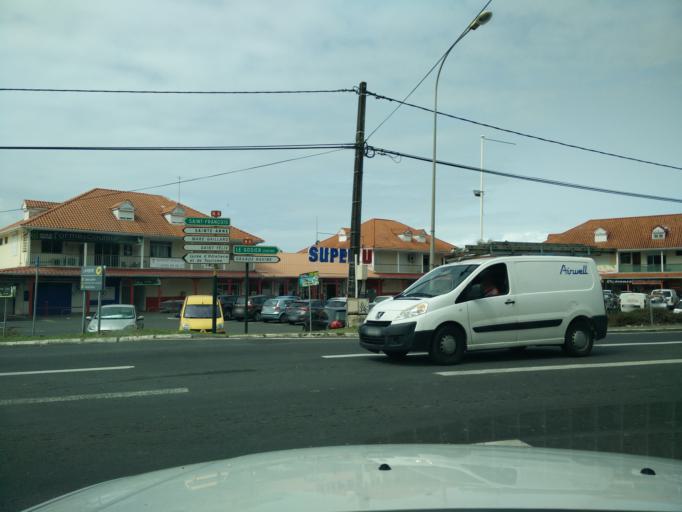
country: GP
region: Guadeloupe
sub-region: Guadeloupe
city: Le Gosier
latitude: 16.2084
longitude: -61.4659
